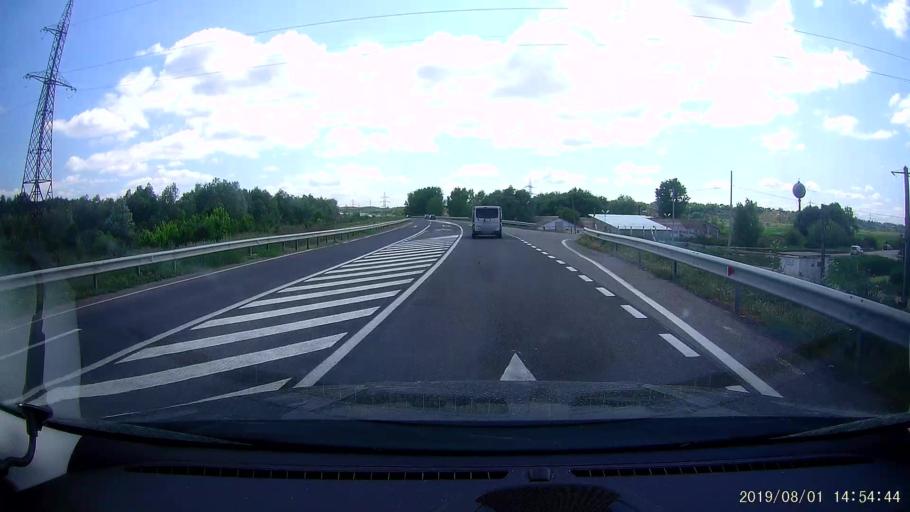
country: RO
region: Braila
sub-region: Municipiul Braila
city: Braila
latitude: 45.3141
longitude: 27.9845
